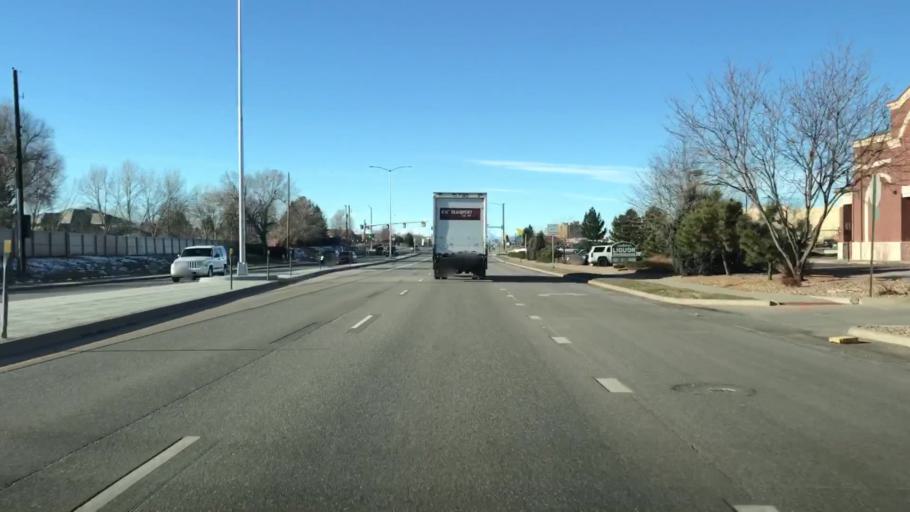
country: US
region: Colorado
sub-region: Arapahoe County
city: Glendale
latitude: 39.6881
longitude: -104.8878
